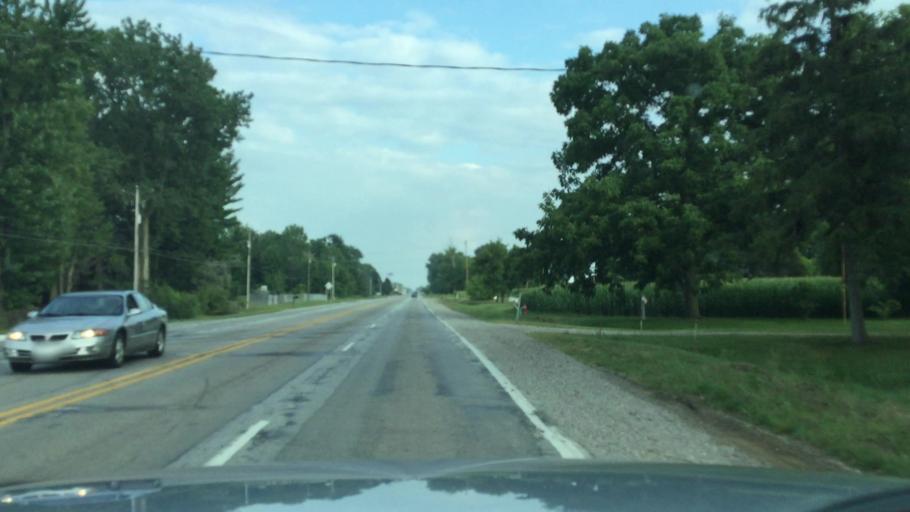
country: US
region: Michigan
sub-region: Saginaw County
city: Birch Run
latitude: 43.2613
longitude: -83.7778
